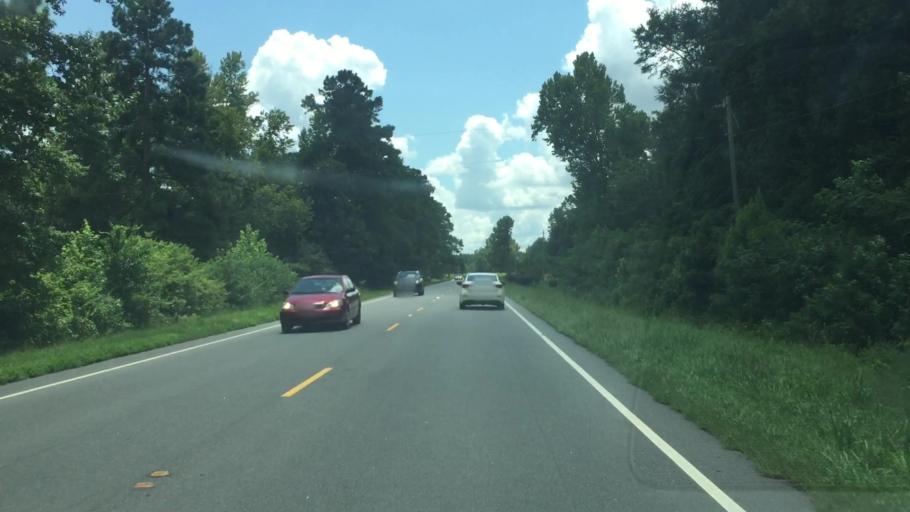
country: US
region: North Carolina
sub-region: Columbus County
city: Tabor City
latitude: 34.1912
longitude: -78.8363
